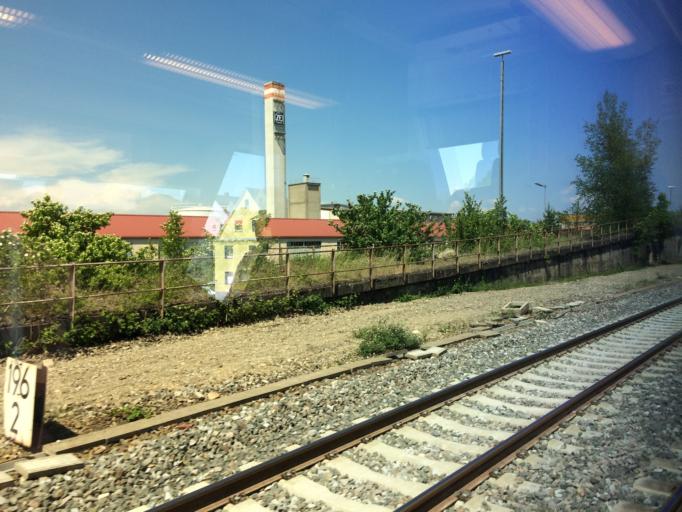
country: DE
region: Baden-Wuerttemberg
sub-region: Tuebingen Region
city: Friedrichshafen
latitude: 47.6574
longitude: 9.4900
